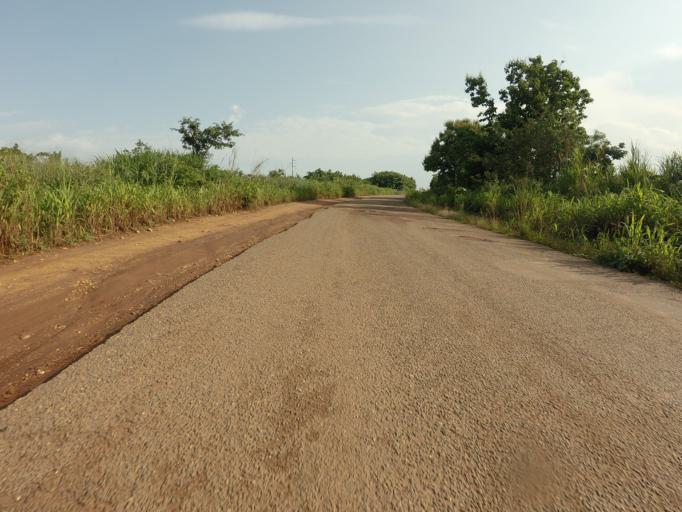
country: GH
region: Volta
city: Hohoe
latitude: 7.0841
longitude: 0.4442
